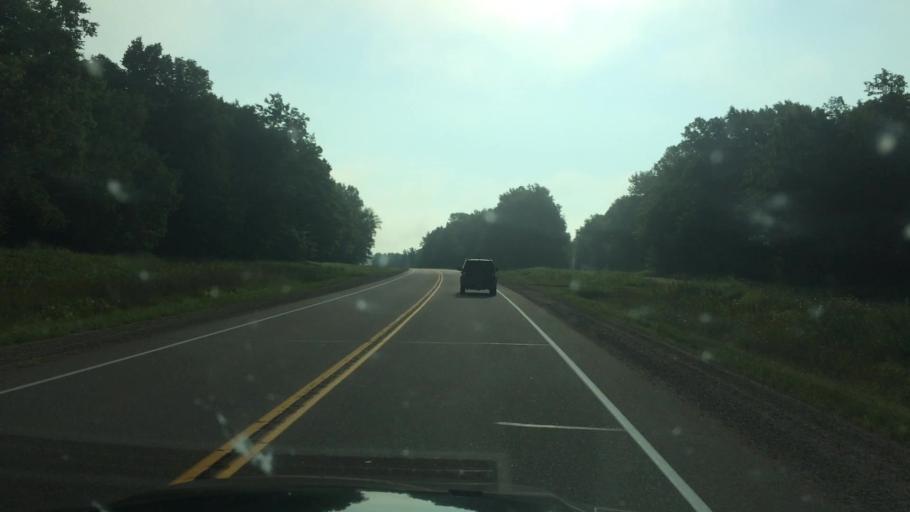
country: US
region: Wisconsin
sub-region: Langlade County
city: Antigo
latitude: 45.1439
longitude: -89.2984
